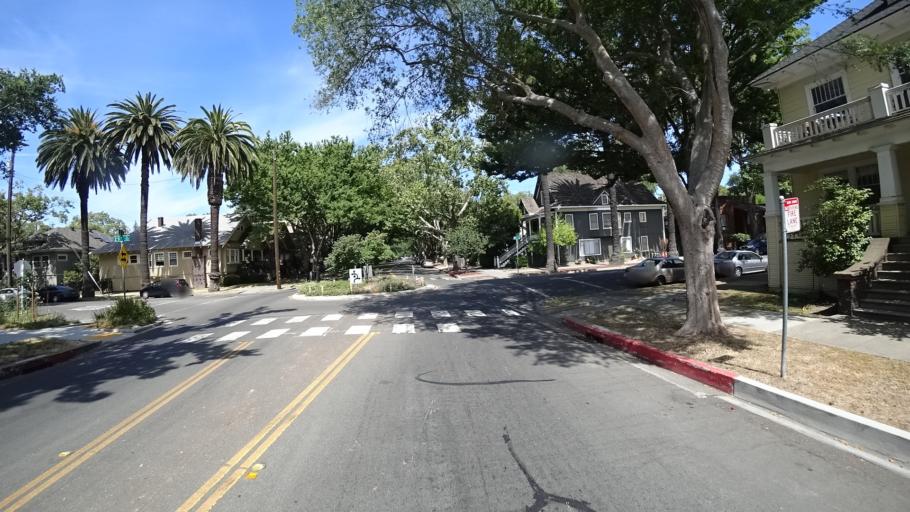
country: US
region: California
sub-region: Sacramento County
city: Sacramento
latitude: 38.5781
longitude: -121.4715
